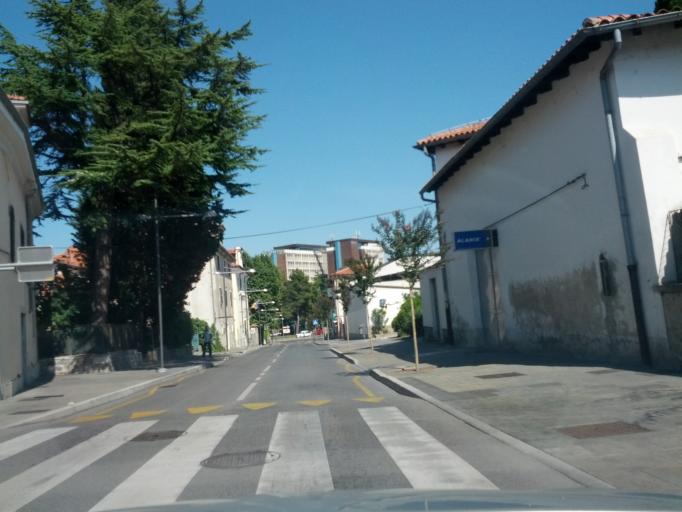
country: SI
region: Koper-Capodistria
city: Koper
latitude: 45.5483
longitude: 13.7341
